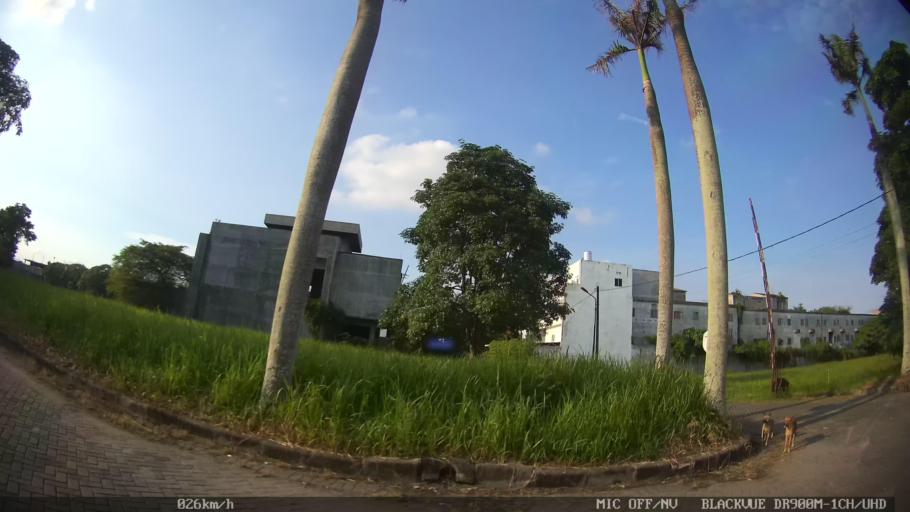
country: ID
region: North Sumatra
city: Medan
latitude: 3.6257
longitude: 98.6431
